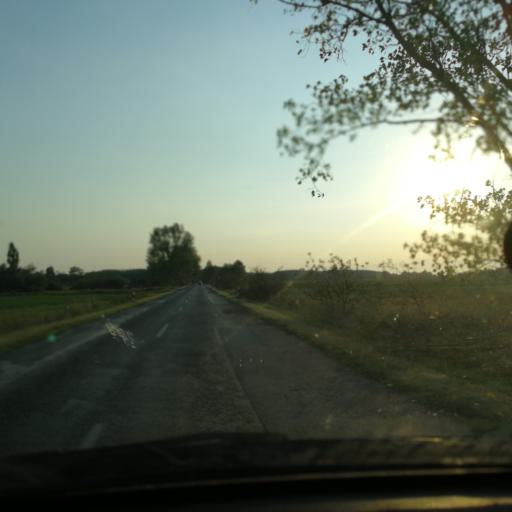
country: HU
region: Bacs-Kiskun
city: Szank
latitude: 46.4544
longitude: 19.6308
